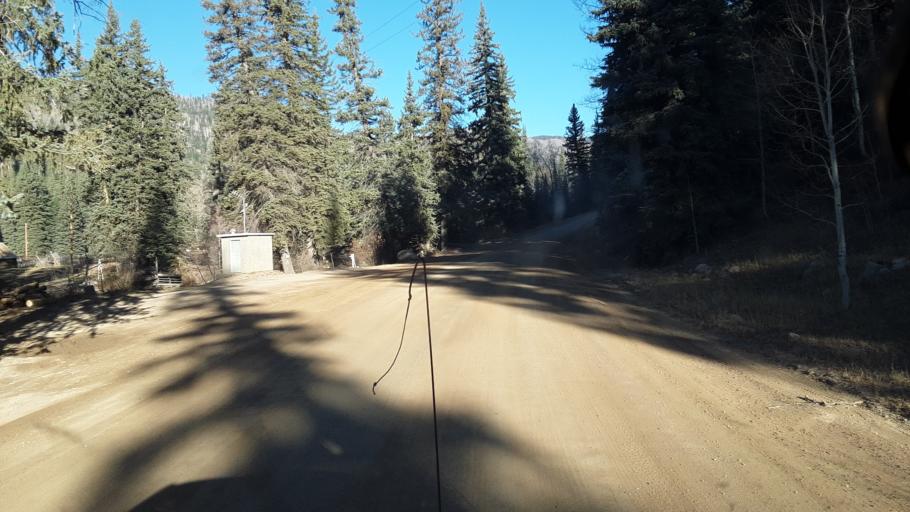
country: US
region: Colorado
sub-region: La Plata County
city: Bayfield
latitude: 37.4271
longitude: -107.6745
